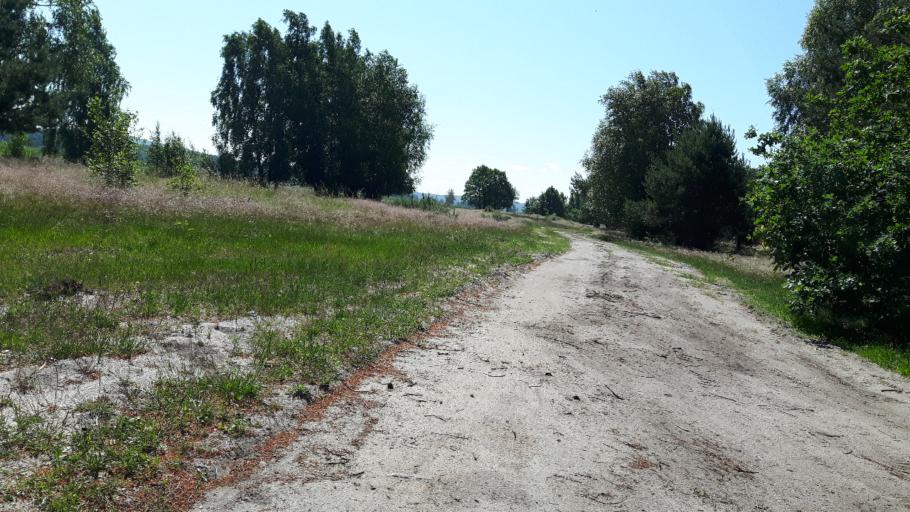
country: PL
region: Pomeranian Voivodeship
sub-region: Powiat slupski
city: Smoldzino
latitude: 54.6748
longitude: 17.1575
